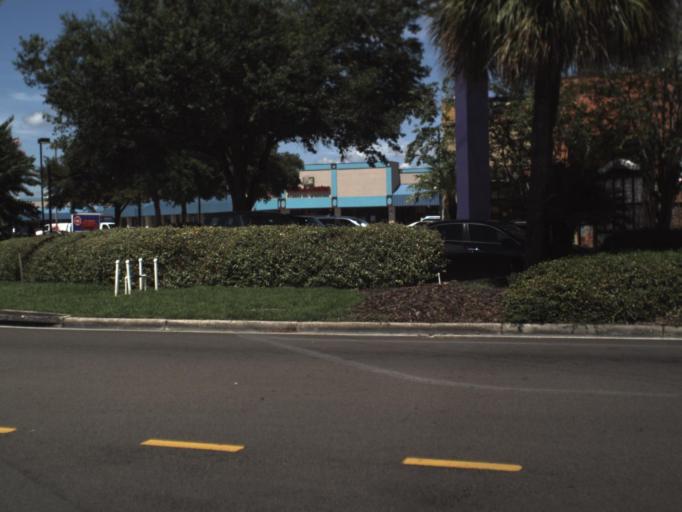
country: US
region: Florida
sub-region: Polk County
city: Auburndale
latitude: 28.0550
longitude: -81.7781
